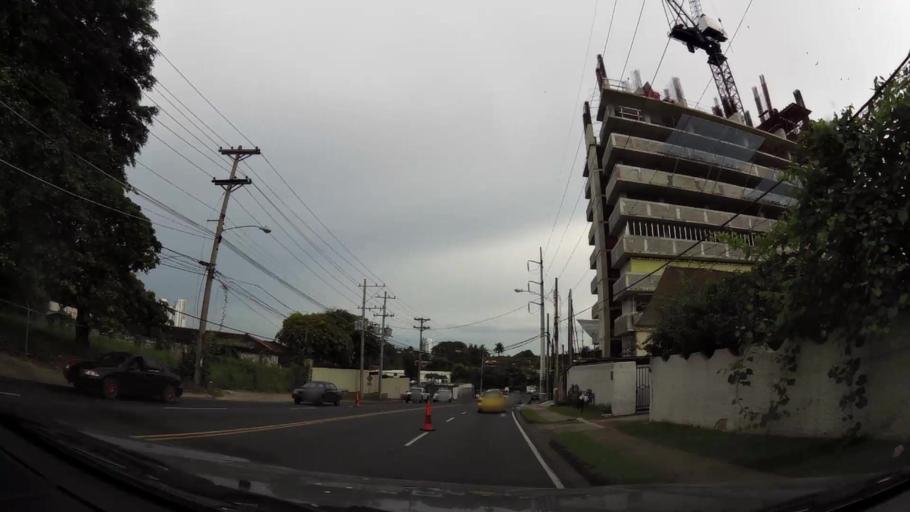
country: PA
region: Panama
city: Panama
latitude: 8.9954
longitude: -79.4991
